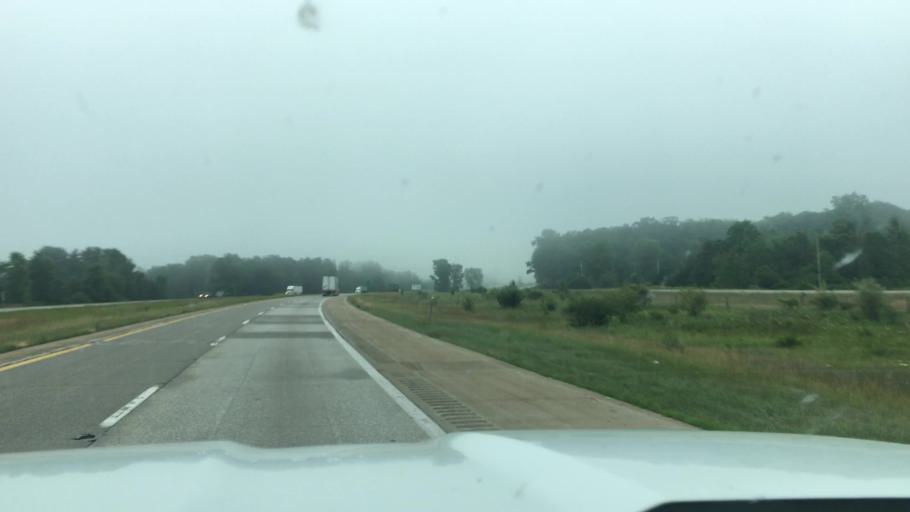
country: US
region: Michigan
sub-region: Shiawassee County
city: Perry
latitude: 42.8257
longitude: -84.2629
